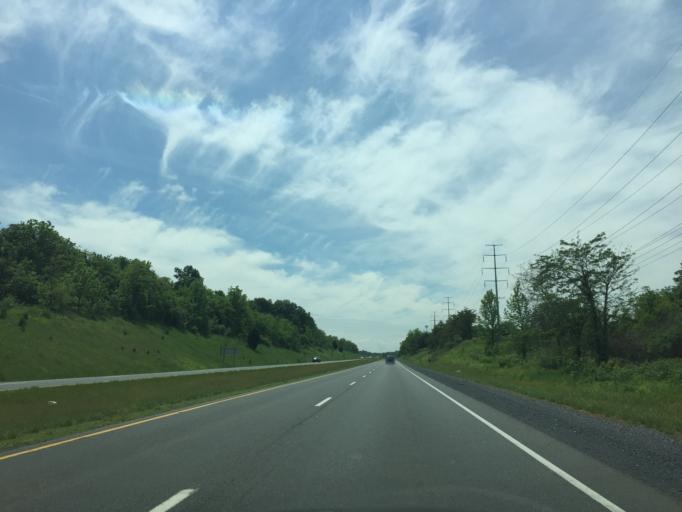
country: US
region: Virginia
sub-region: City of Winchester
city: Winchester
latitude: 39.1697
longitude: -78.2083
